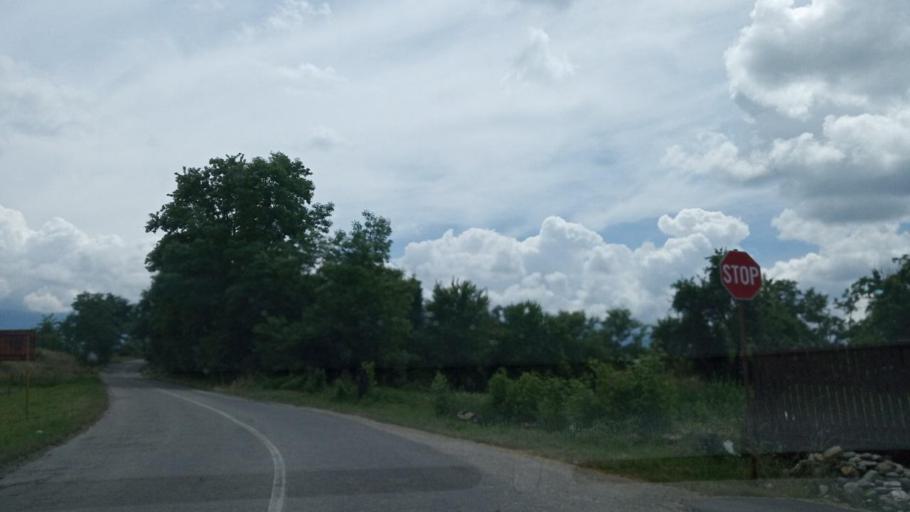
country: RO
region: Sibiu
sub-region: Comuna Porumbacu de Jos
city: Porumbacu de Jos
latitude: 45.7498
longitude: 24.4613
